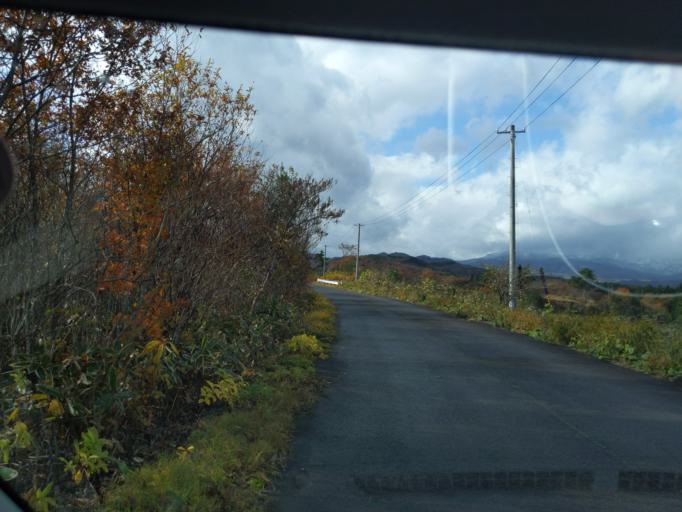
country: JP
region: Iwate
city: Mizusawa
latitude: 39.1043
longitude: 140.9723
